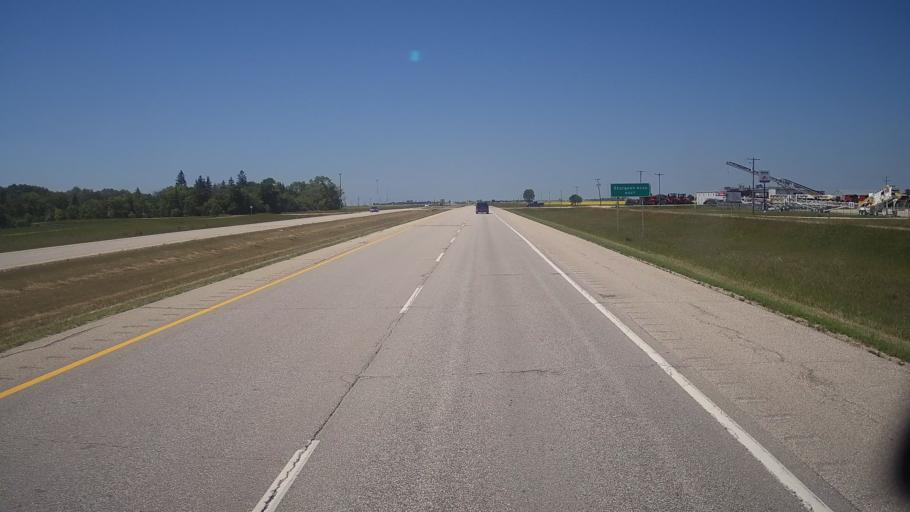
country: CA
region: Manitoba
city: Stonewall
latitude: 49.9900
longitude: -97.2724
